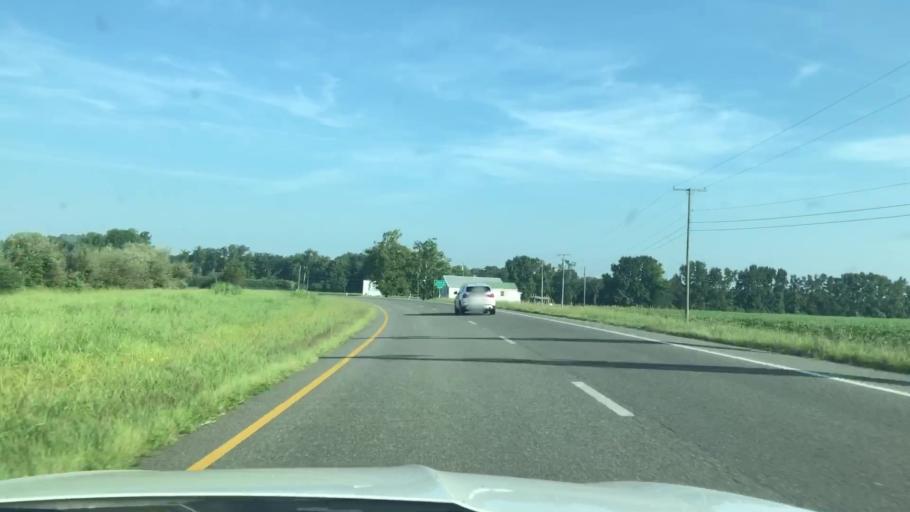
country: US
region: Virginia
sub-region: Middlesex County
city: Saluda
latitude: 37.7136
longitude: -76.6929
